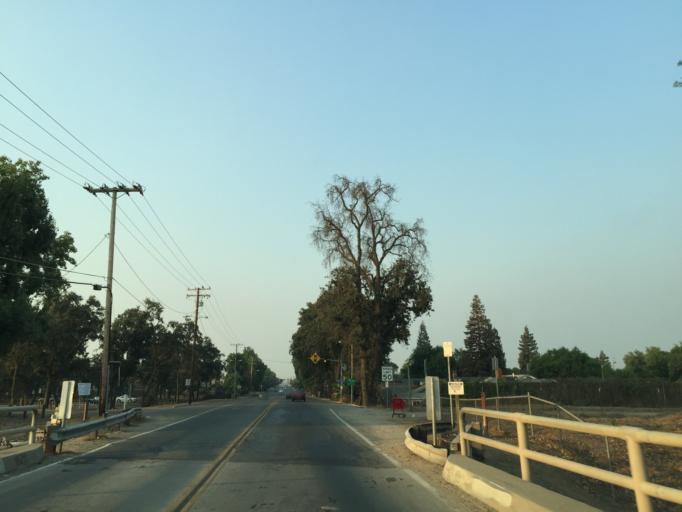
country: US
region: California
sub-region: Tulare County
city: Visalia
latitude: 36.3532
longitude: -119.2790
